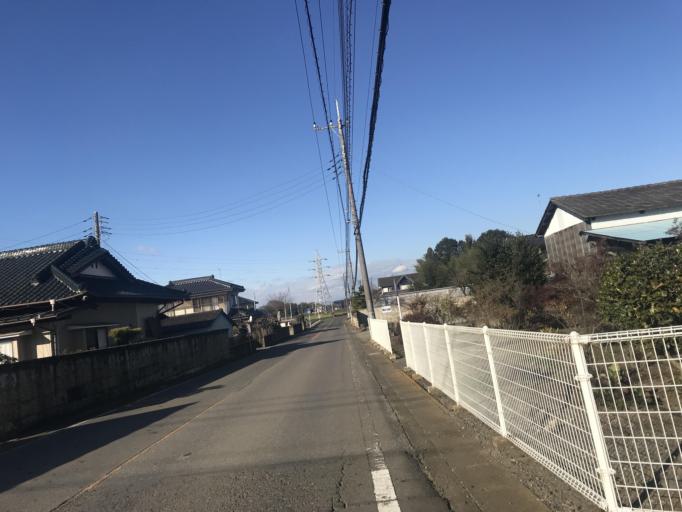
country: JP
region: Tochigi
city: Kaminokawa
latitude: 36.4080
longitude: 139.8775
